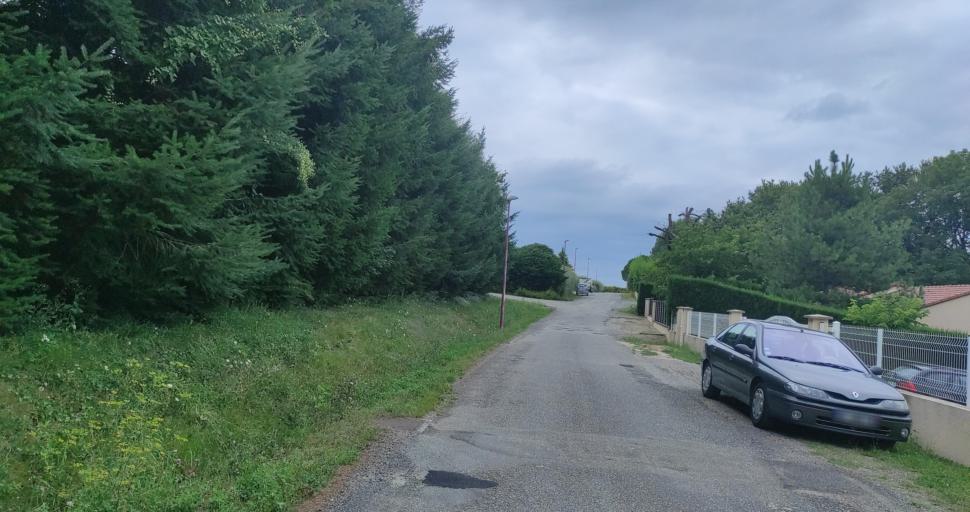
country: FR
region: Midi-Pyrenees
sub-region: Departement de l'Aveyron
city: Villeneuve
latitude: 44.3992
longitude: 2.0745
